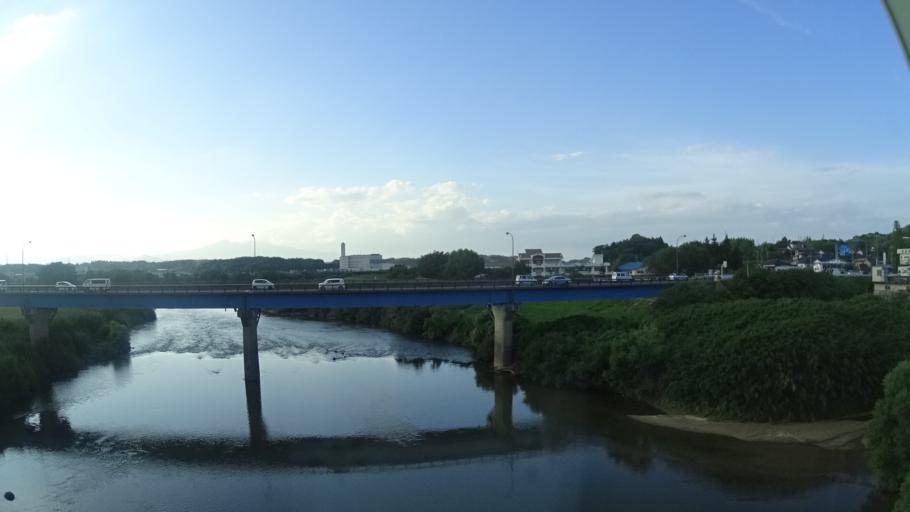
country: JP
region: Fukushima
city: Koriyama
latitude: 37.4219
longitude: 140.4153
